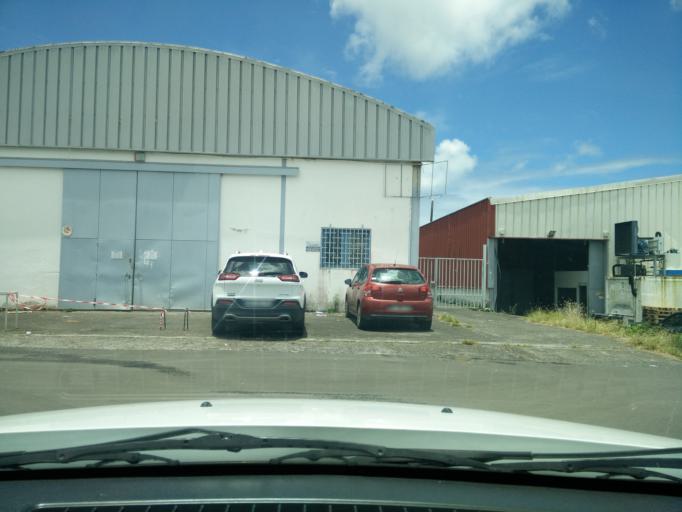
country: GP
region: Guadeloupe
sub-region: Guadeloupe
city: Les Abymes
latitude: 16.2577
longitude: -61.5104
